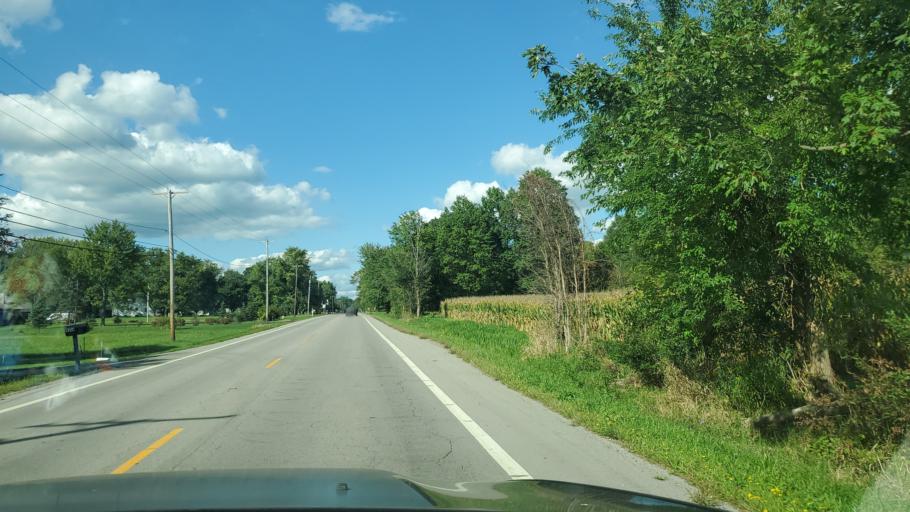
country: US
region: Ohio
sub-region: Mahoning County
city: Canfield
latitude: 41.0581
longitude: -80.7607
